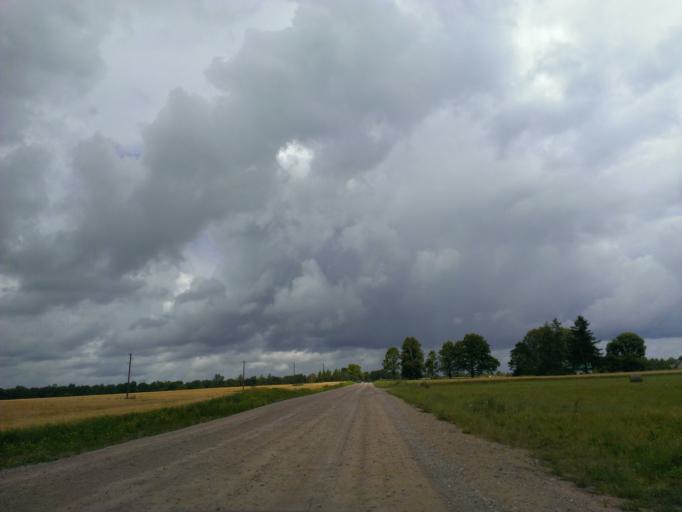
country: LV
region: Sigulda
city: Sigulda
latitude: 57.1922
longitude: 24.9429
